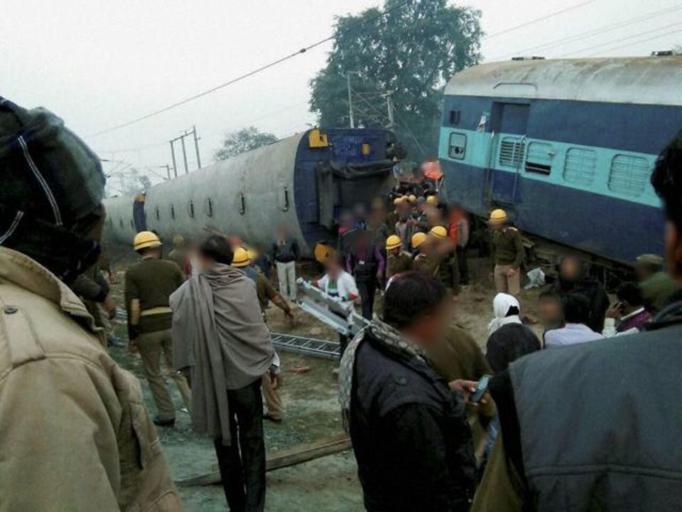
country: IN
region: Uttar Pradesh
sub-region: Kanpur Dehat
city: Rura
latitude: 26.4799
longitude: 79.9782
